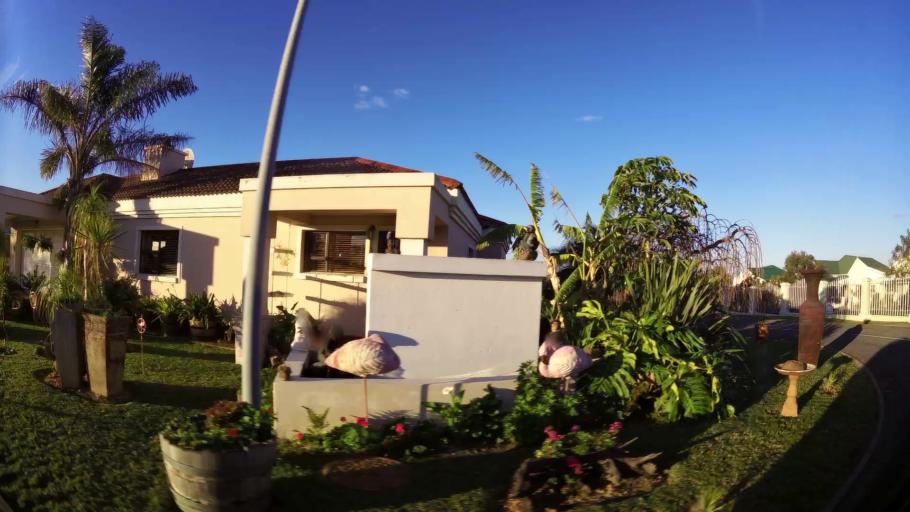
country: ZA
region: Western Cape
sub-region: Eden District Municipality
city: Riversdale
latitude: -34.0830
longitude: 21.2431
